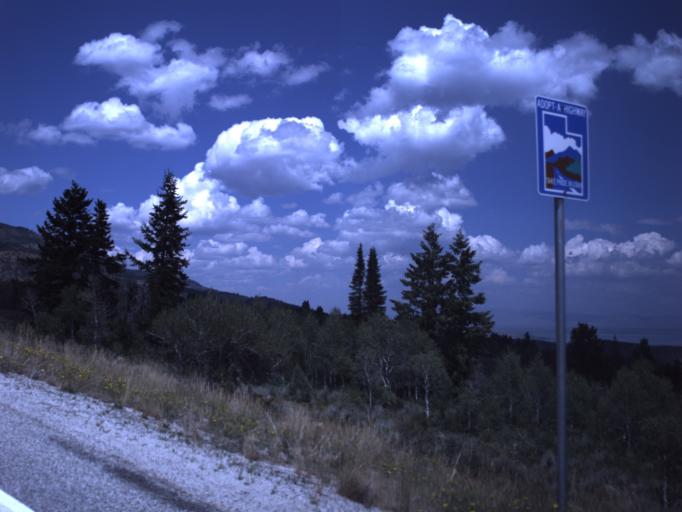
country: US
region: Idaho
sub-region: Bear Lake County
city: Paris
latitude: 41.9313
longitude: -111.4458
